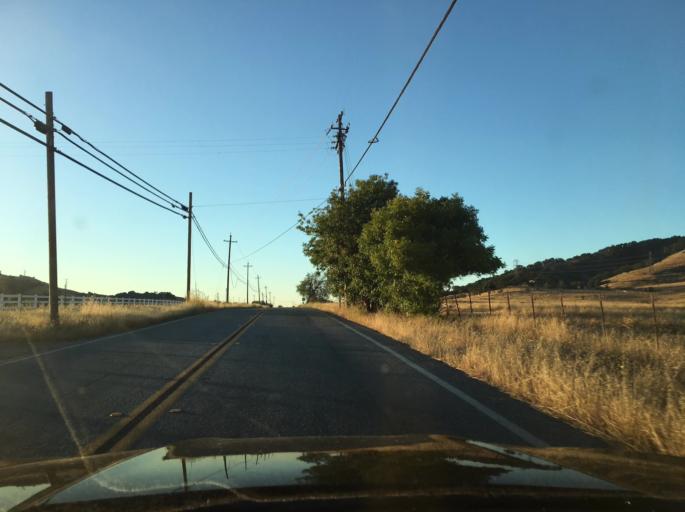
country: US
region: California
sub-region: Santa Clara County
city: Seven Trees
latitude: 37.1961
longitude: -121.8110
